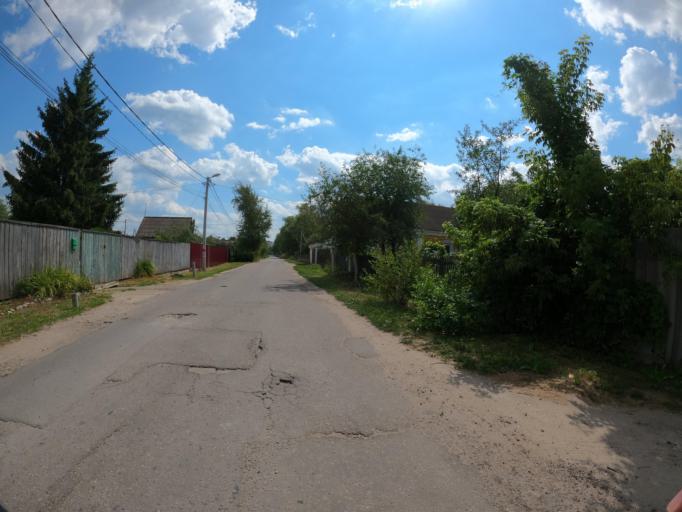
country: RU
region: Moskovskaya
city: Lopatinskiy
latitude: 55.2814
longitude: 38.7433
